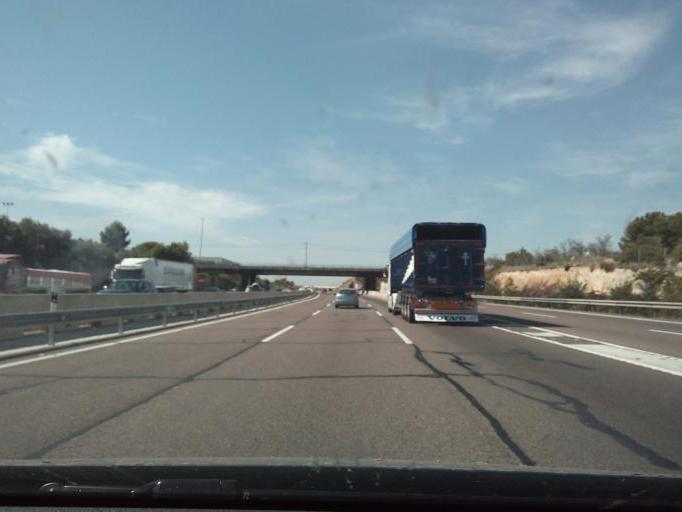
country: ES
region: Valencia
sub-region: Provincia de Valencia
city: Manises
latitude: 39.5226
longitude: -0.4742
